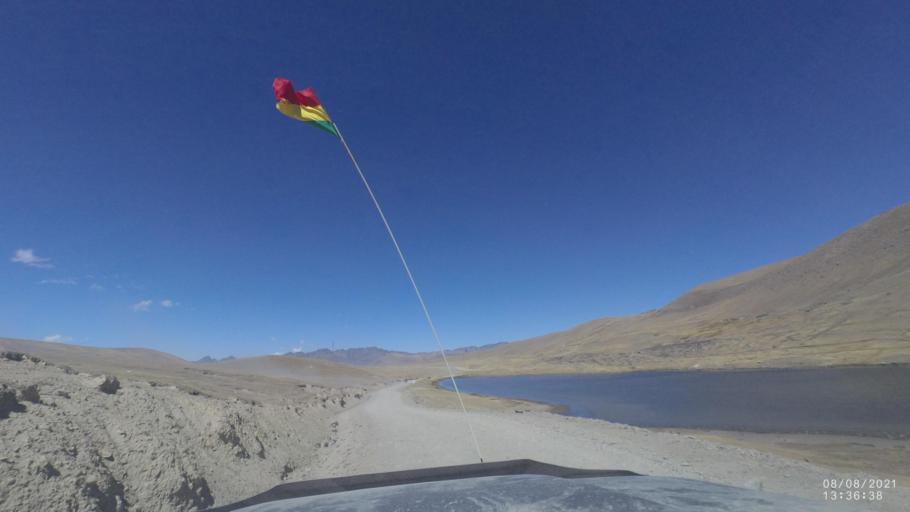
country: BO
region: Cochabamba
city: Colchani
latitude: -17.0742
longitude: -66.5015
